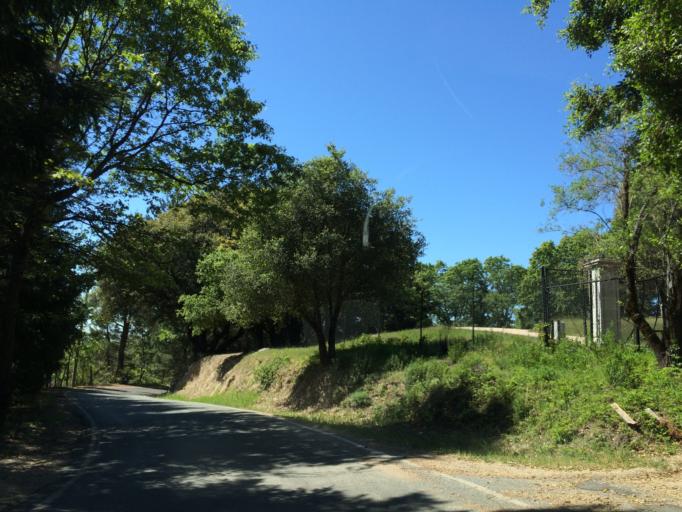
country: US
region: California
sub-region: Santa Clara County
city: Monte Sereno
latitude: 37.1999
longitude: -122.0426
